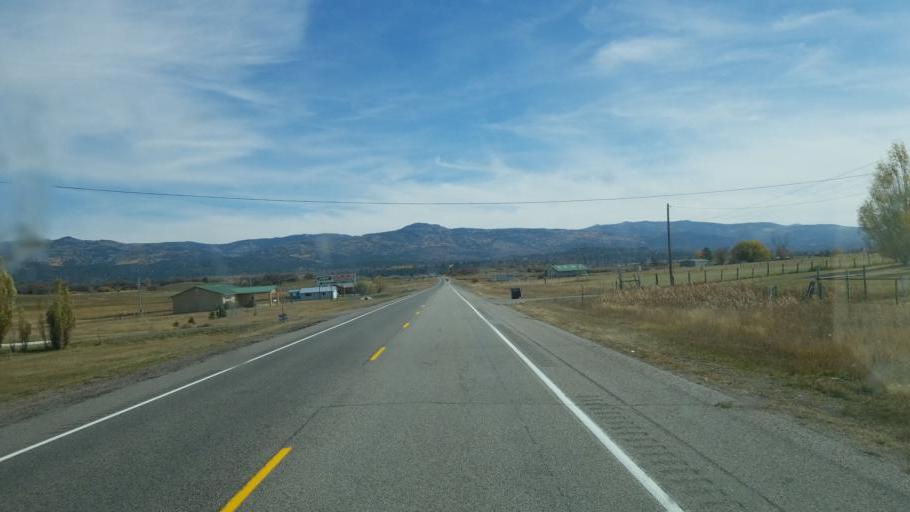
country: US
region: New Mexico
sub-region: Rio Arriba County
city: Chama
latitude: 36.8854
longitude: -106.6122
